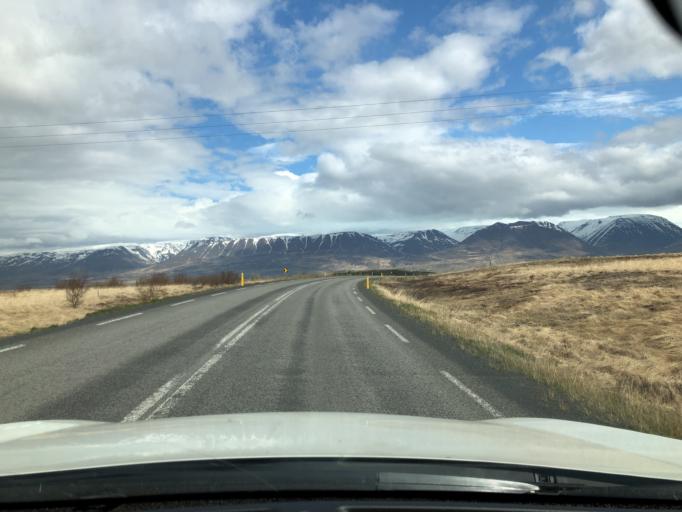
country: IS
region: Northwest
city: Saudarkrokur
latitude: 65.5483
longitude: -19.4897
